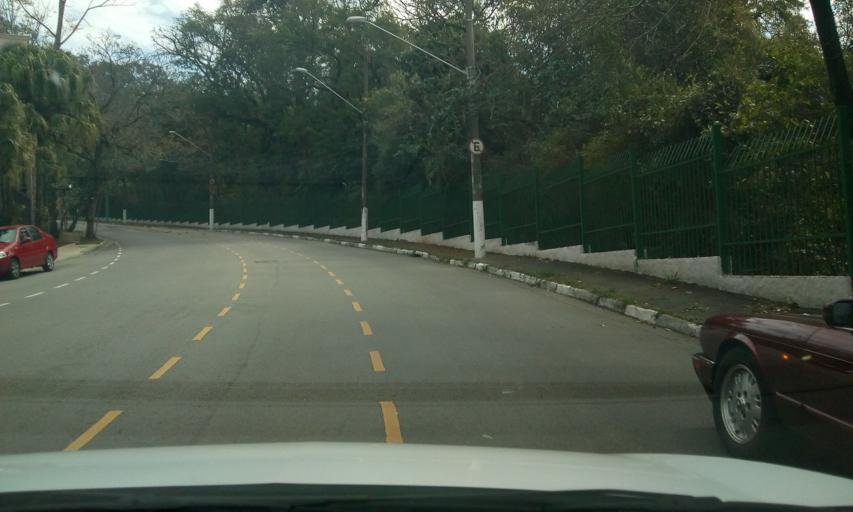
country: BR
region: Sao Paulo
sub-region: Sao Paulo
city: Sao Paulo
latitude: -23.5886
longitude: -46.7032
